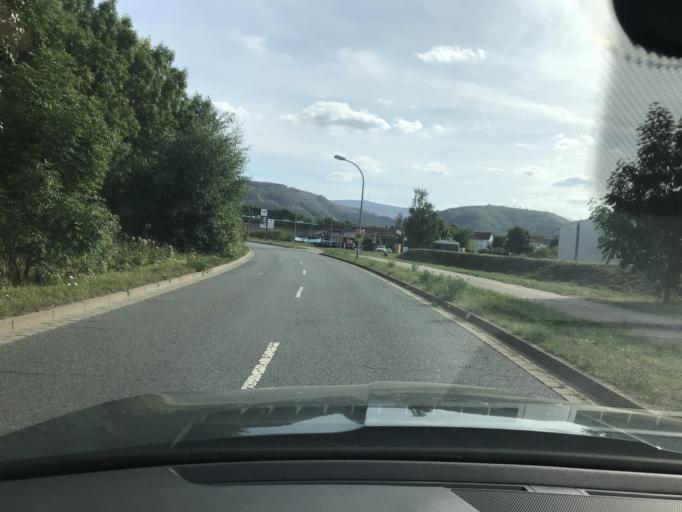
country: DE
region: Saxony-Anhalt
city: Ilsenburg
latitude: 51.8743
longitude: 10.6933
